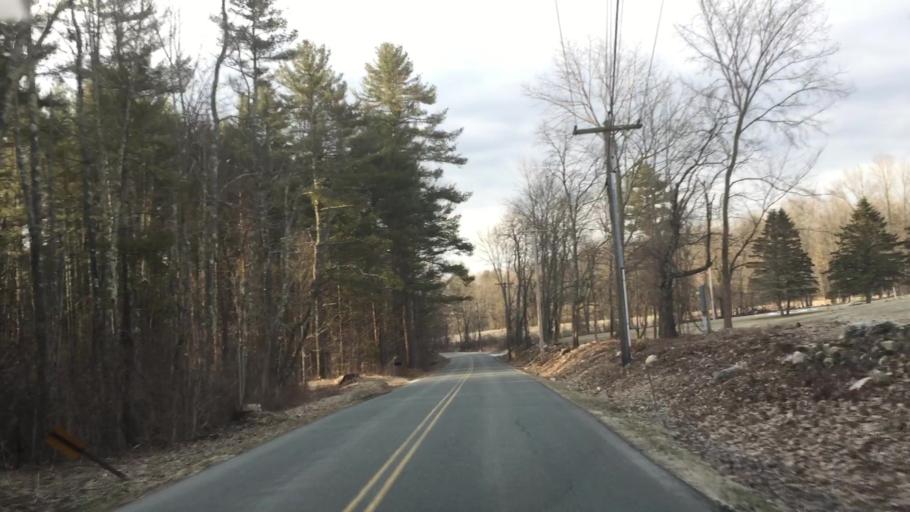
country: US
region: Massachusetts
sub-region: Berkshire County
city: New Marlborough
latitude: 42.1523
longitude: -73.2773
